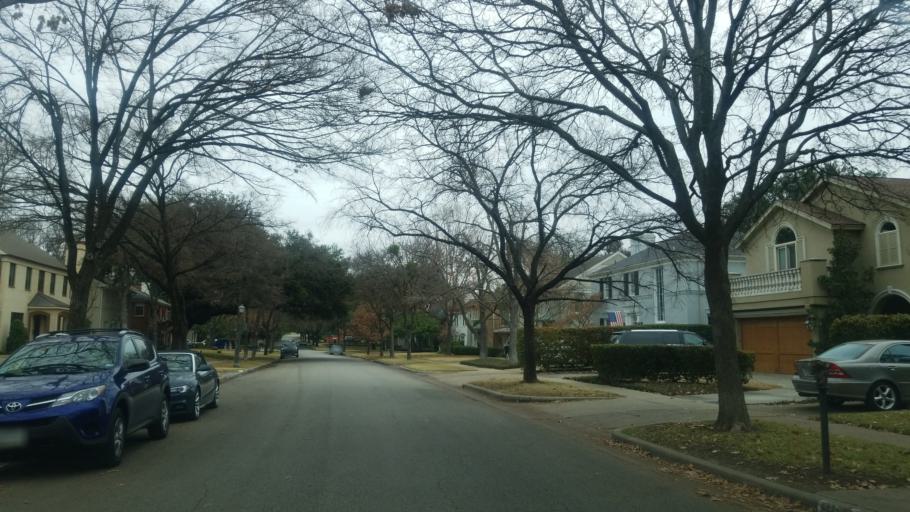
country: US
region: Texas
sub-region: Dallas County
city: Highland Park
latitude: 32.8267
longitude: -96.8134
